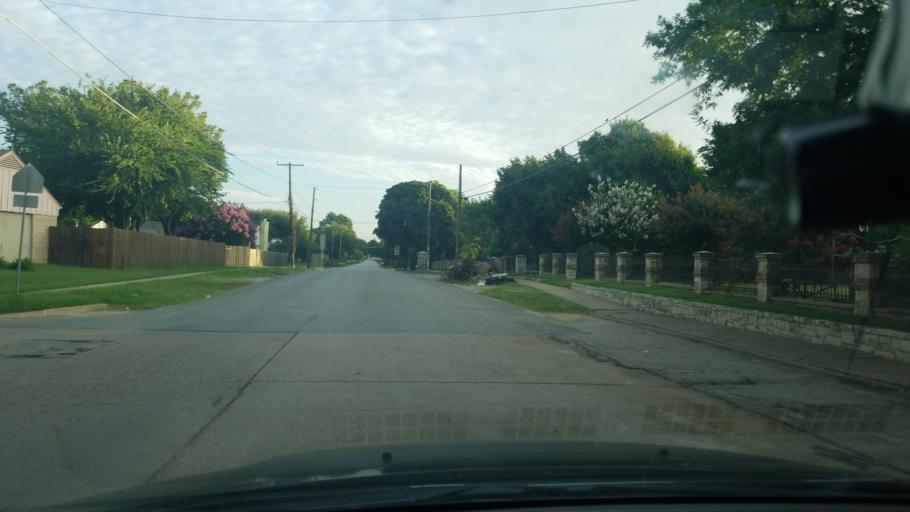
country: US
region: Texas
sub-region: Dallas County
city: Balch Springs
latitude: 32.7411
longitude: -96.6398
